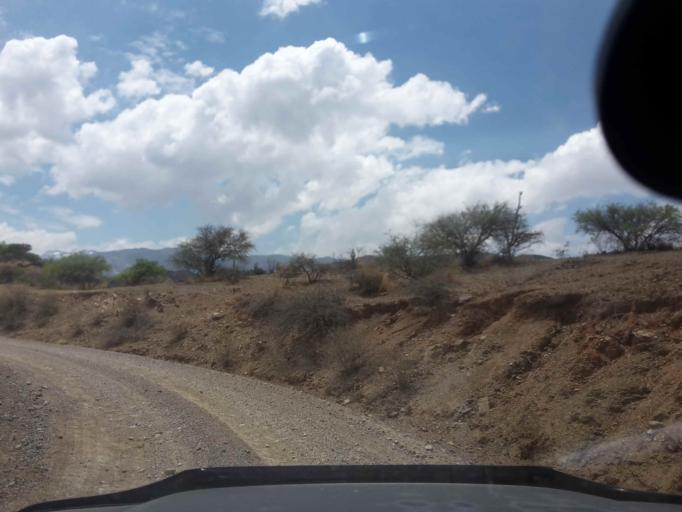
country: BO
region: Cochabamba
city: Sipe Sipe
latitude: -17.5446
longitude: -66.4795
